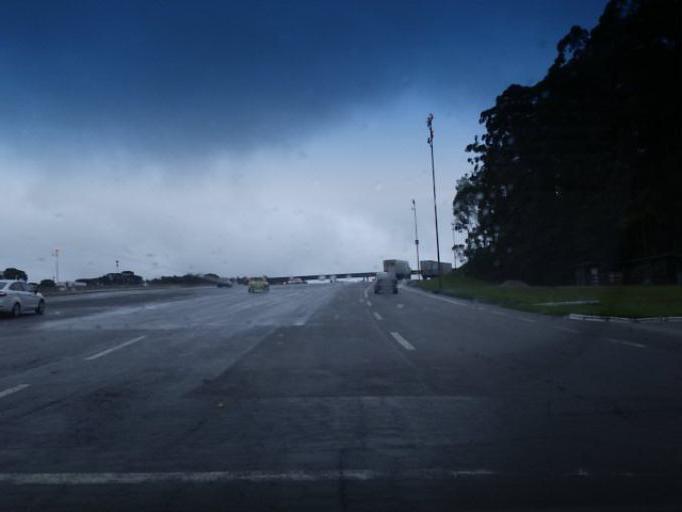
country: BR
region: Parana
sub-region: Sao Jose Dos Pinhais
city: Sao Jose dos Pinhais
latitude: -25.7499
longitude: -49.1283
